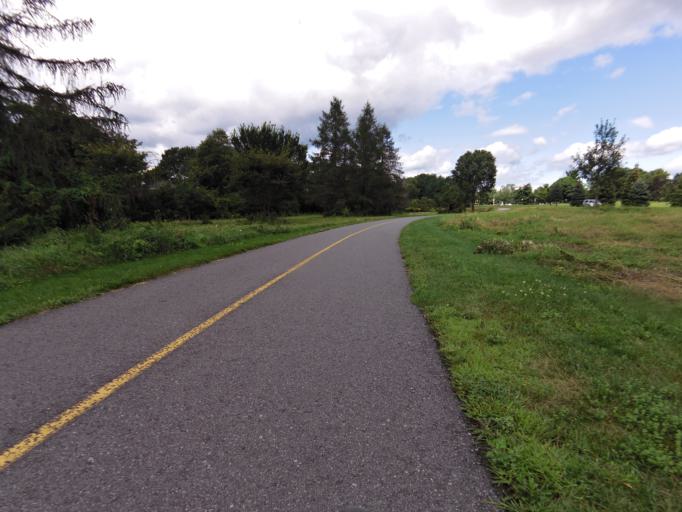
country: CA
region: Ontario
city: Ottawa
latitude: 45.4404
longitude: -75.6375
